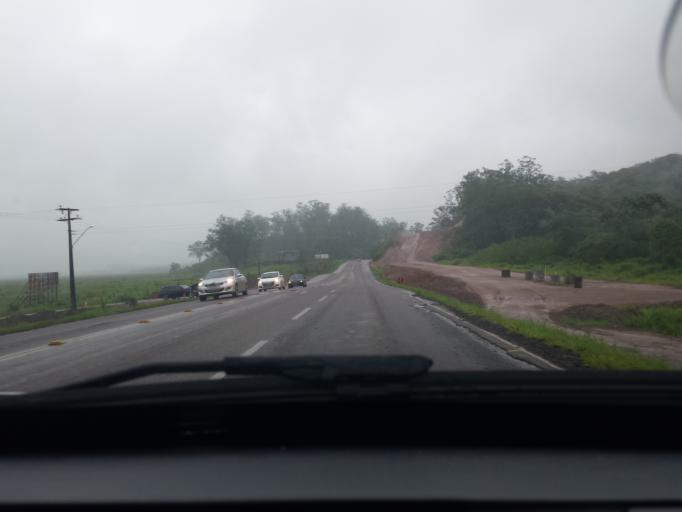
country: BR
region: Santa Catarina
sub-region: Itajai
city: Itajai
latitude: -26.8388
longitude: -48.7787
